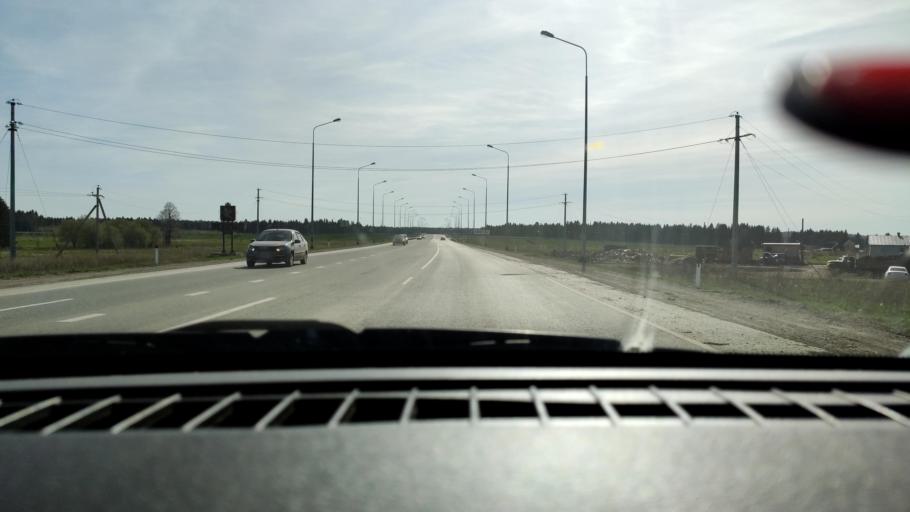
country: RU
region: Perm
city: Kukushtan
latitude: 57.6383
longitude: 56.4656
